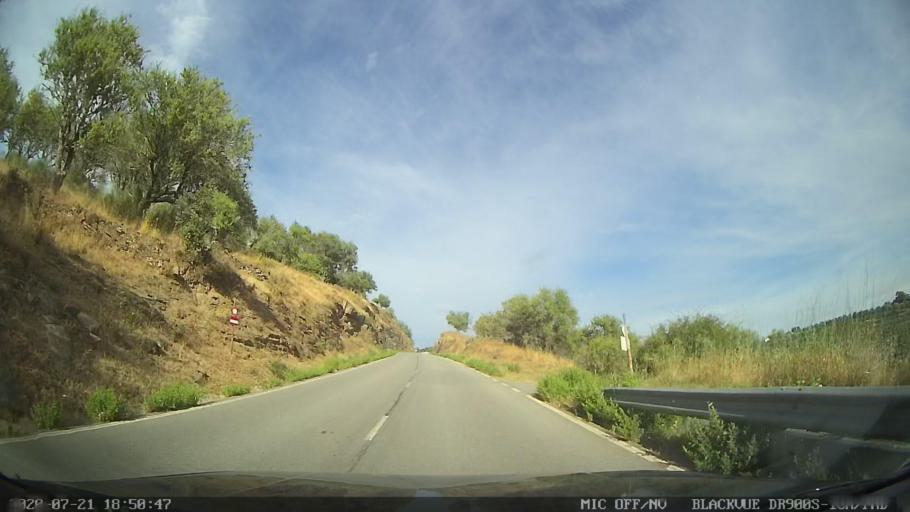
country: PT
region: Viseu
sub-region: Sao Joao da Pesqueira
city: Sao Joao da Pesqueira
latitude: 41.1426
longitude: -7.4281
